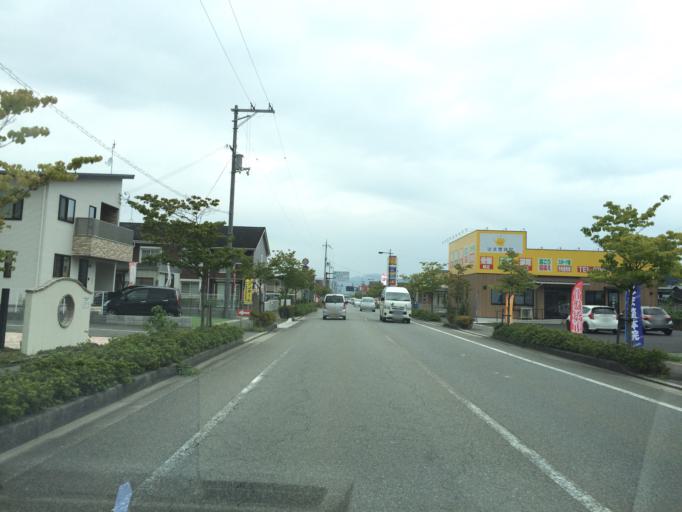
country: JP
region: Hyogo
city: Toyooka
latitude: 35.5333
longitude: 134.8081
